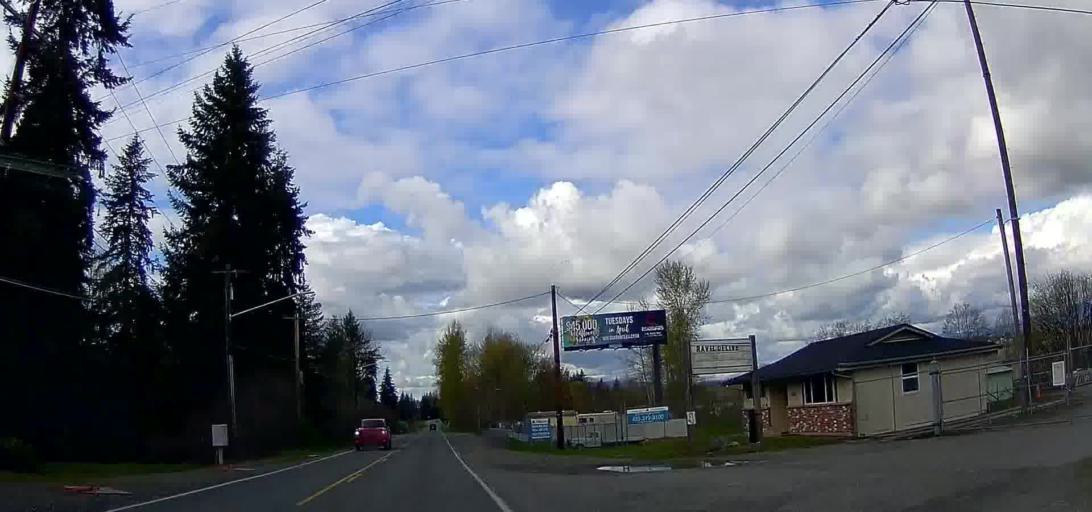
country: US
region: Washington
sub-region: Snohomish County
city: Smokey Point
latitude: 48.1708
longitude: -122.1886
